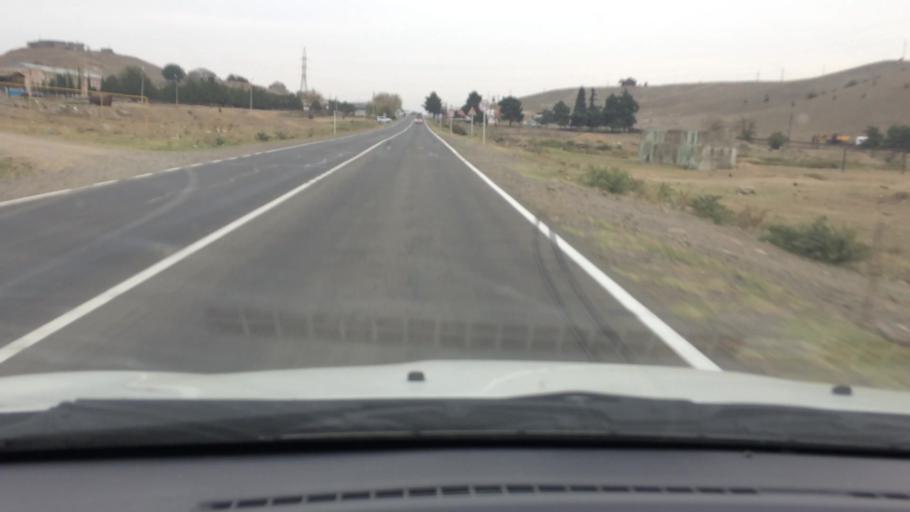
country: GE
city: Naghvarevi
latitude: 41.3604
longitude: 44.8343
